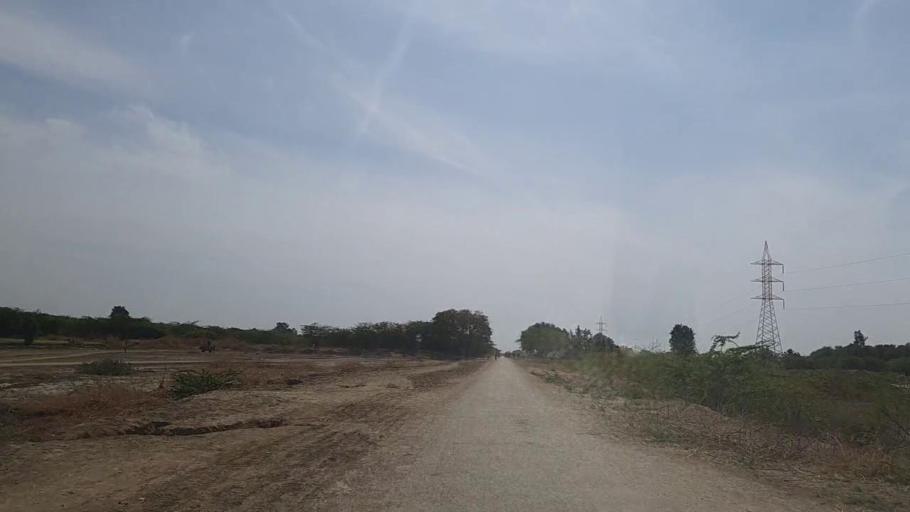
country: PK
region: Sindh
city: Kunri
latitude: 25.1912
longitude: 69.4611
